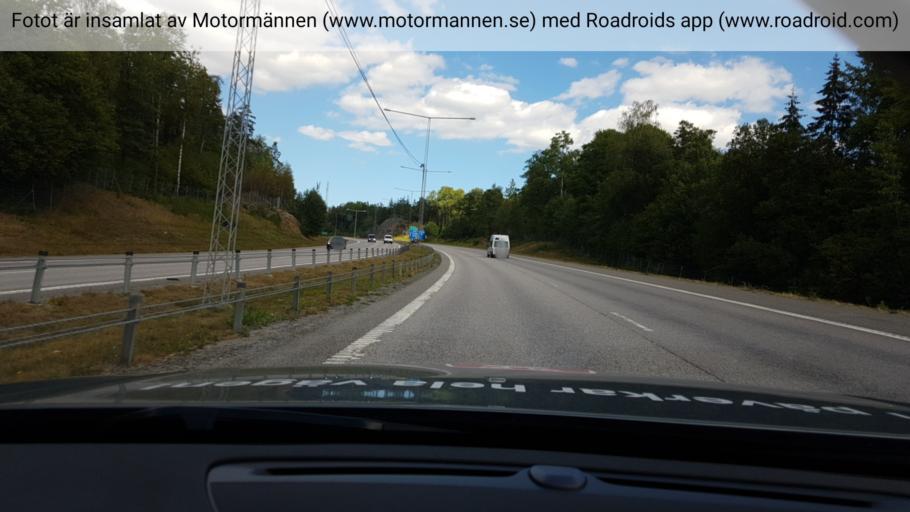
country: SE
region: Stockholm
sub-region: Haninge Kommun
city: Haninge
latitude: 59.1364
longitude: 18.1580
